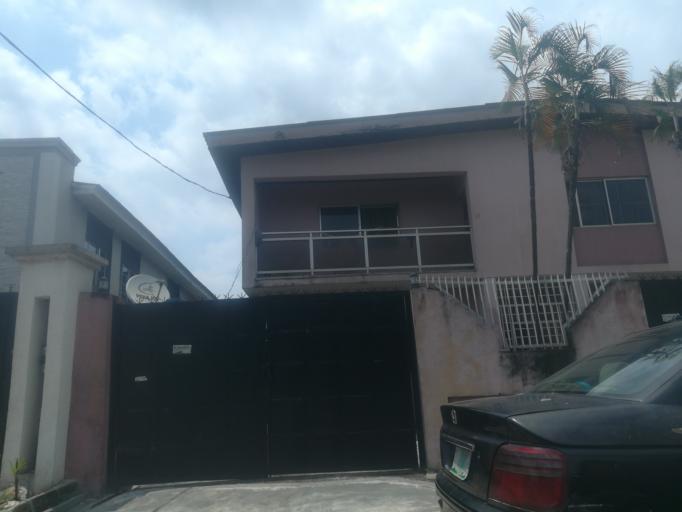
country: NG
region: Lagos
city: Ojota
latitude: 6.5619
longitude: 3.3939
